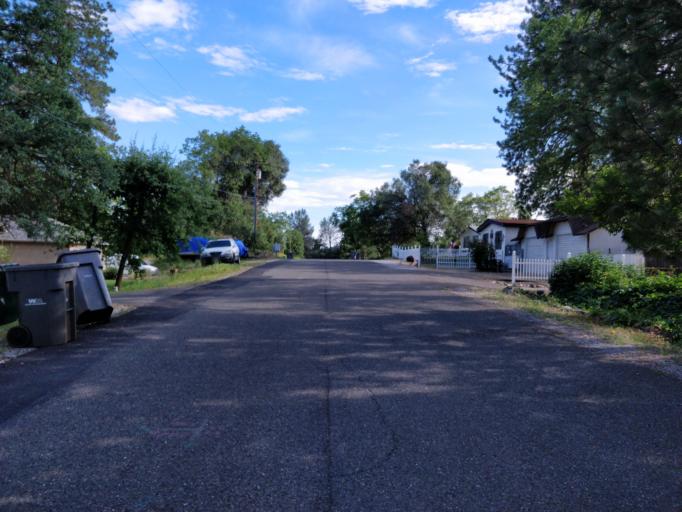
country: US
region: California
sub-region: Shasta County
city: Shasta Lake
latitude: 40.6853
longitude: -122.3696
